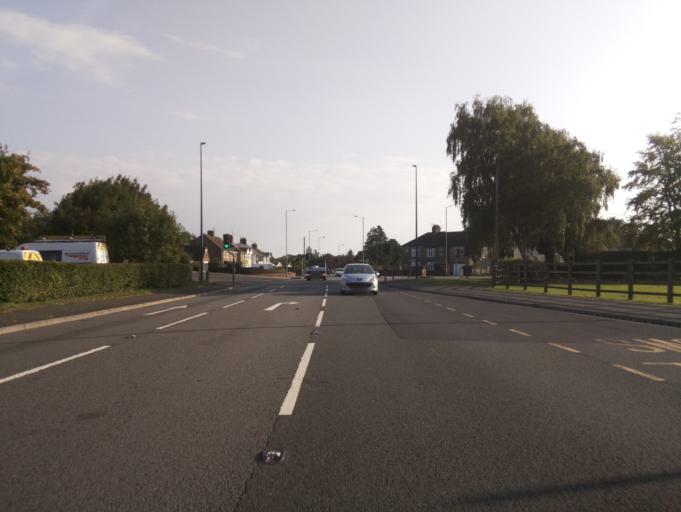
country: GB
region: Wales
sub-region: Torfaen County Borough
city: Cwmbran
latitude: 51.6704
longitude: -3.0181
